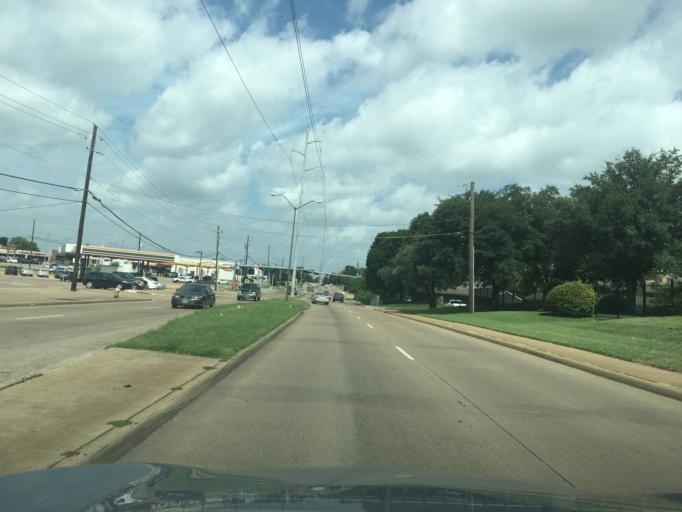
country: US
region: Texas
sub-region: Dallas County
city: Richardson
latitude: 32.9222
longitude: -96.7163
